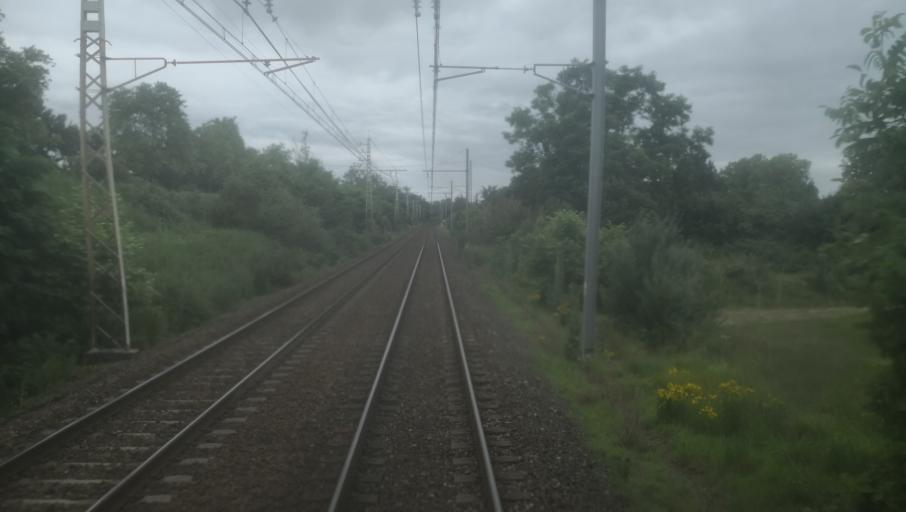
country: FR
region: Midi-Pyrenees
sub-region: Departement de la Haute-Garonne
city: Saint-Jory
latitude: 43.7589
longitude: 1.3596
